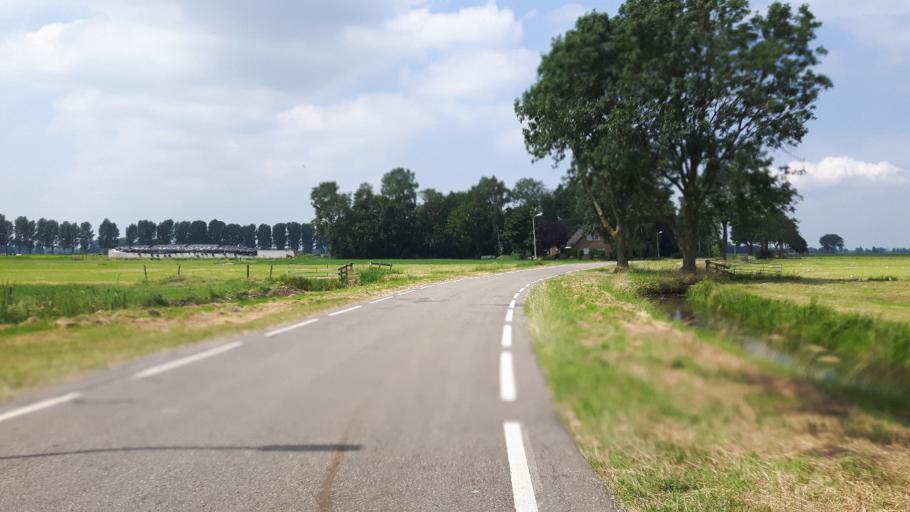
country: NL
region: Utrecht
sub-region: Gemeente Lopik
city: Lopik
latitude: 51.9203
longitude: 4.9641
